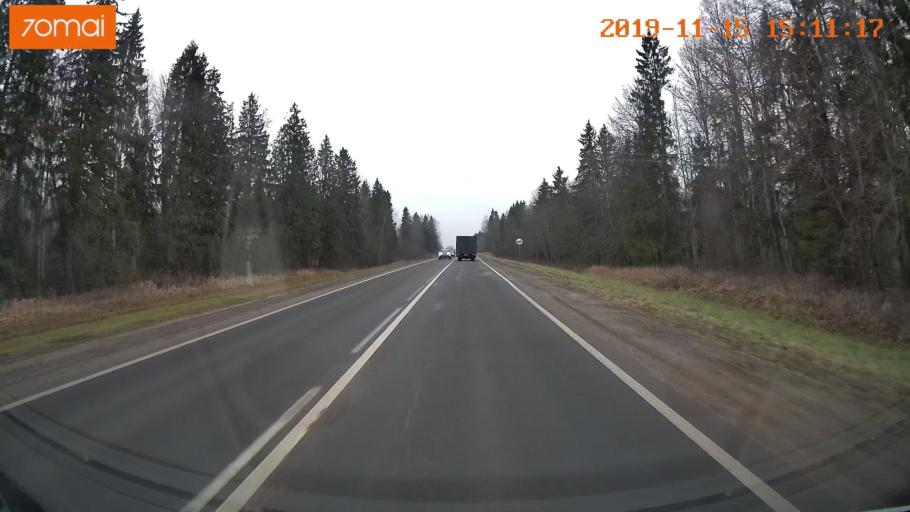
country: RU
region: Jaroslavl
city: Prechistoye
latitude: 58.3383
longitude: 40.2433
